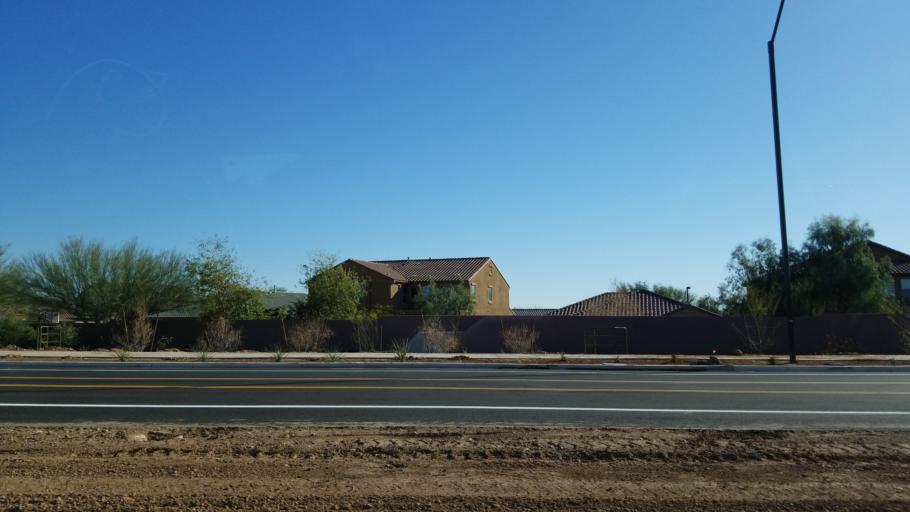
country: US
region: Arizona
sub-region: Maricopa County
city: Cave Creek
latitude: 33.6987
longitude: -111.9793
